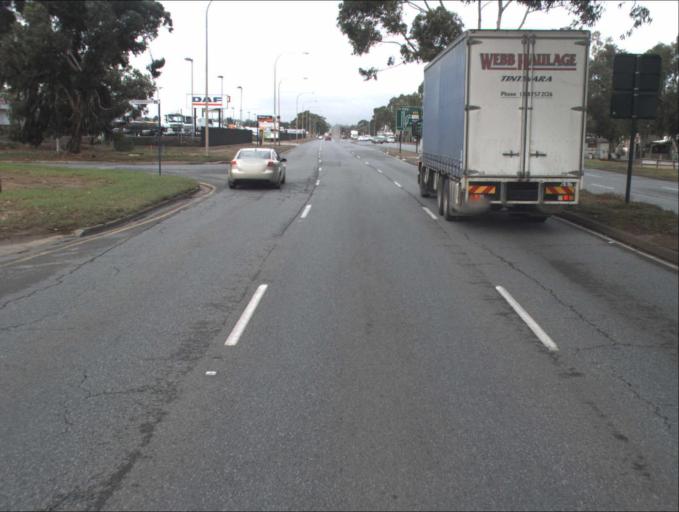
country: AU
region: South Australia
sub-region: Port Adelaide Enfield
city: Enfield
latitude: -34.8333
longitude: 138.5990
